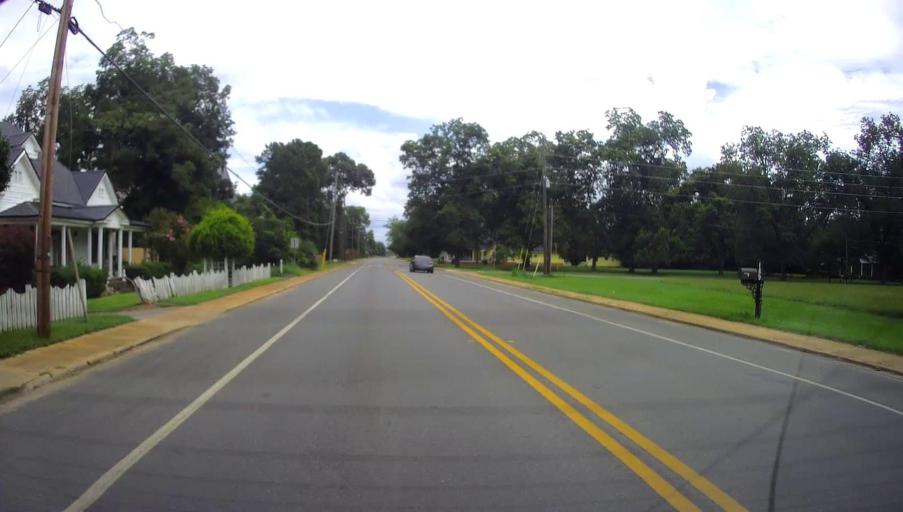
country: US
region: Georgia
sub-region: Schley County
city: Ellaville
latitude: 32.2384
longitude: -84.3056
